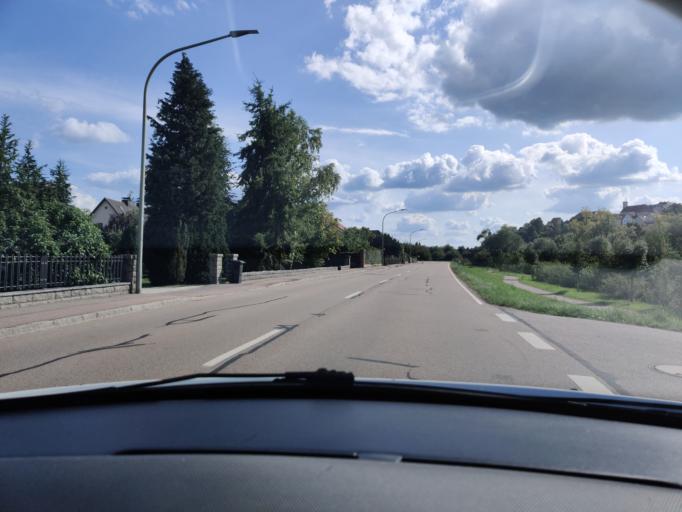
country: DE
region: Bavaria
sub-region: Upper Palatinate
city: Nabburg
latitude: 49.4587
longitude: 12.1849
